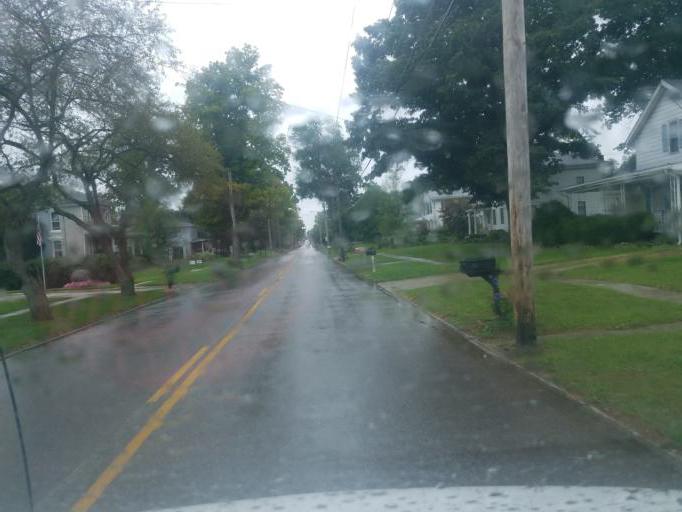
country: US
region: Ohio
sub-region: Medina County
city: Seville
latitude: 41.0101
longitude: -81.8567
